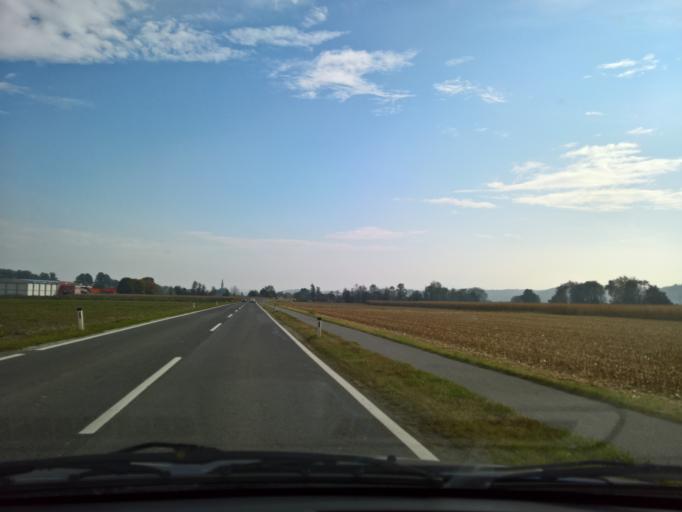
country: AT
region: Styria
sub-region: Politischer Bezirk Deutschlandsberg
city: Gross Sankt Florian
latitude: 46.8228
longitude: 15.2949
